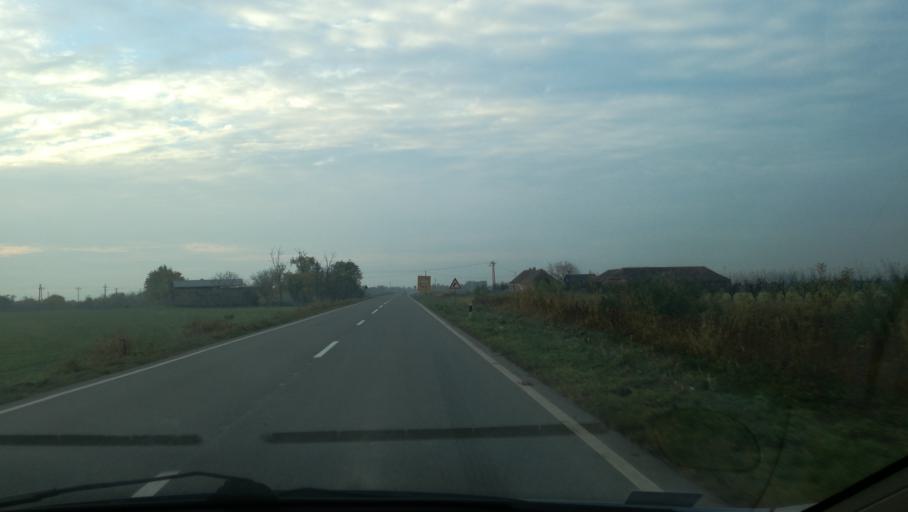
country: RS
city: Banatska Topola
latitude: 45.6949
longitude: 20.4216
